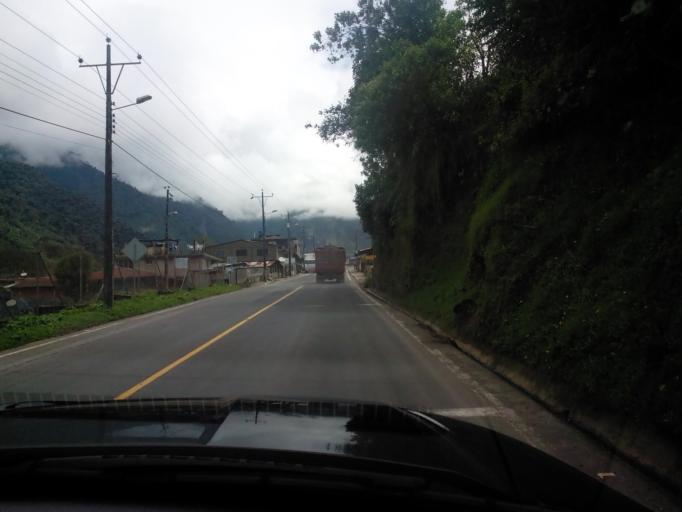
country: EC
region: Pichincha
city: Sangolqui
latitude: -0.4145
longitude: -78.0251
